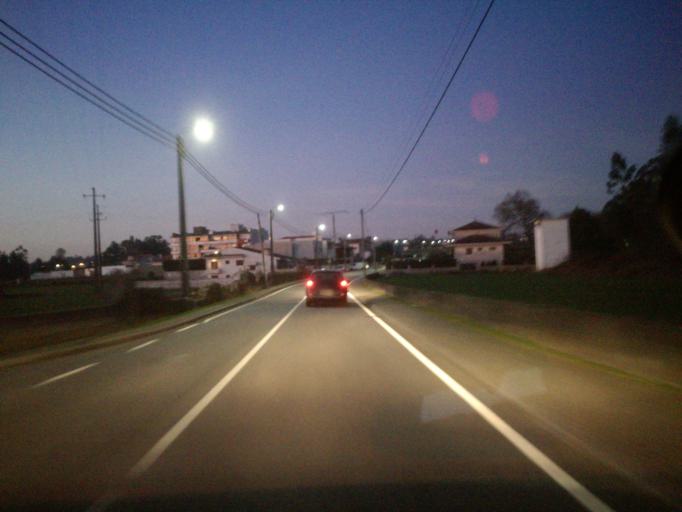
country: PT
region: Porto
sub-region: Maia
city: Nogueira
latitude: 41.2459
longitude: -8.5859
